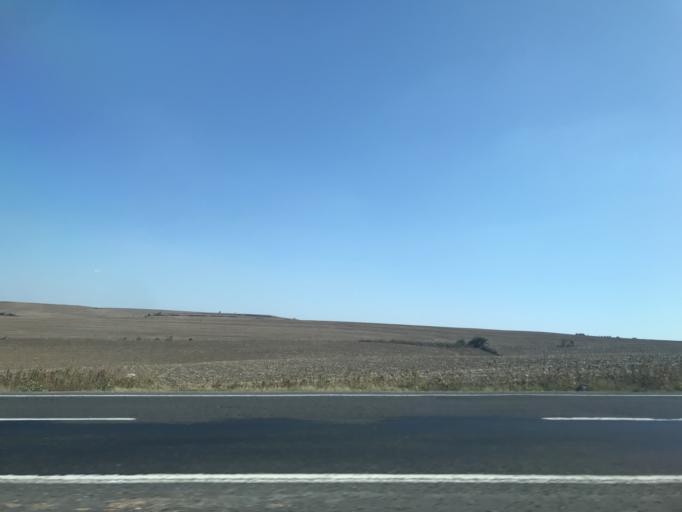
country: TR
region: Tekirdag
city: Muratli
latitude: 41.0963
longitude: 27.4935
